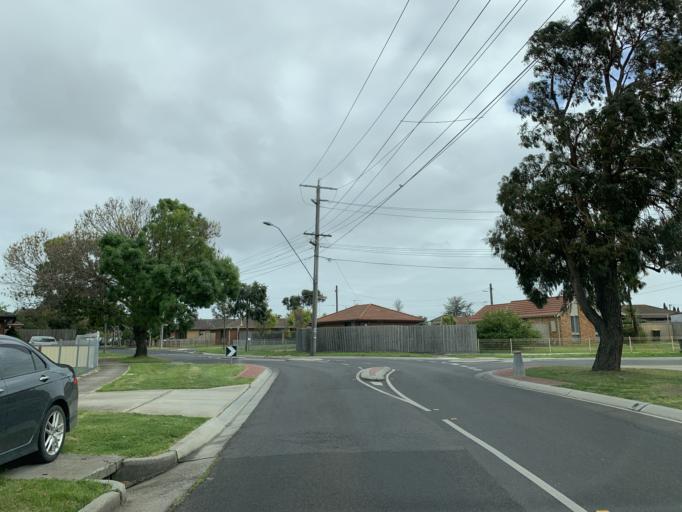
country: AU
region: Victoria
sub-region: Brimbank
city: Kealba
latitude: -37.7515
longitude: 144.8220
